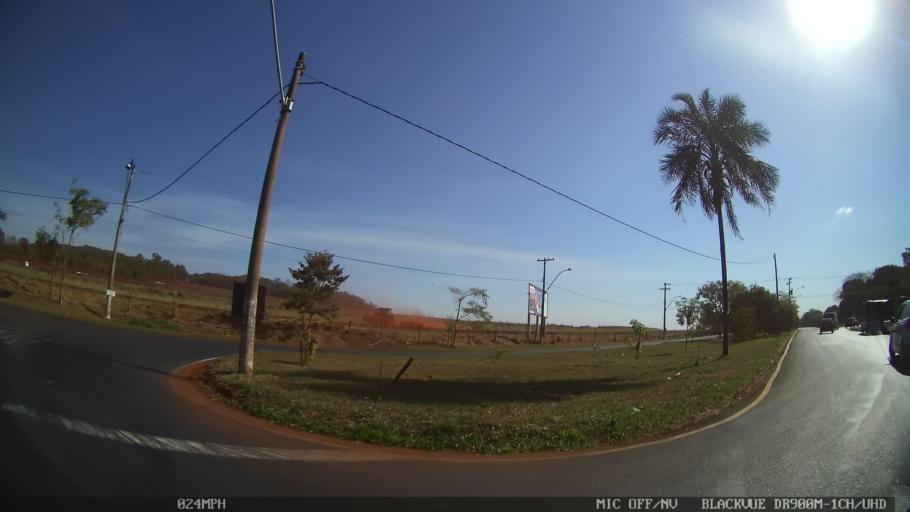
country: BR
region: Sao Paulo
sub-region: Ribeirao Preto
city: Ribeirao Preto
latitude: -21.1596
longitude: -47.7695
